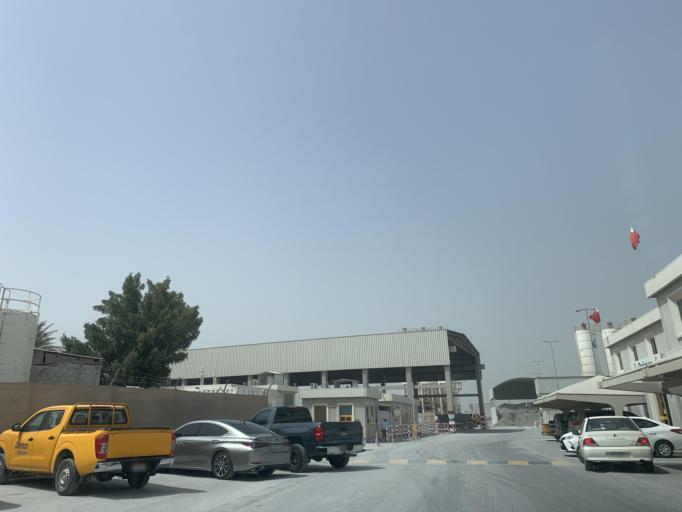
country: BH
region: Northern
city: Madinat `Isa
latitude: 26.1875
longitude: 50.5282
